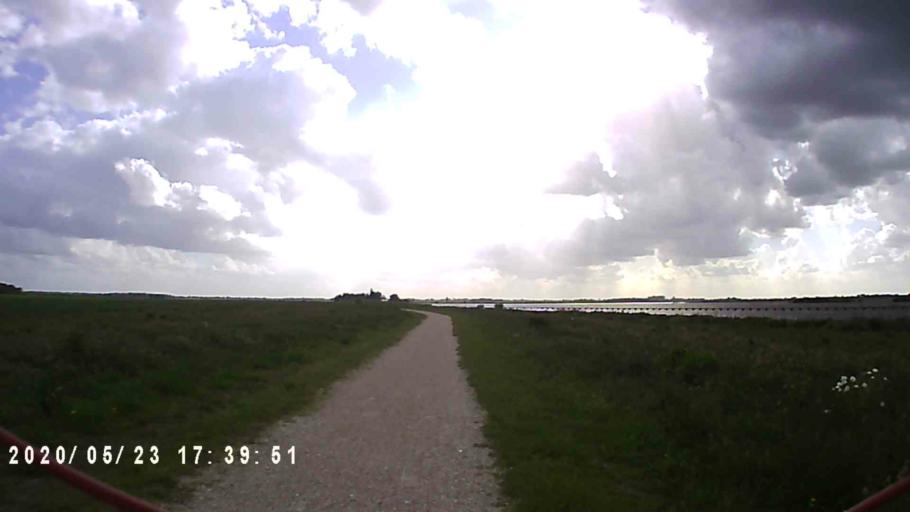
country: NL
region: Groningen
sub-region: Gemeente Slochteren
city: Slochteren
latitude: 53.2428
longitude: 6.7831
